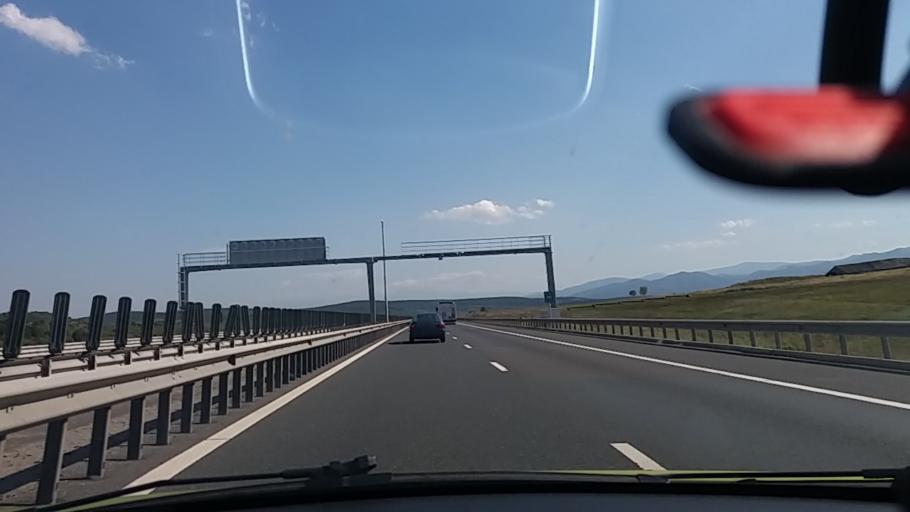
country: RO
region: Sibiu
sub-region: Oras Saliste
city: Saliste
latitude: 45.8036
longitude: 23.9174
